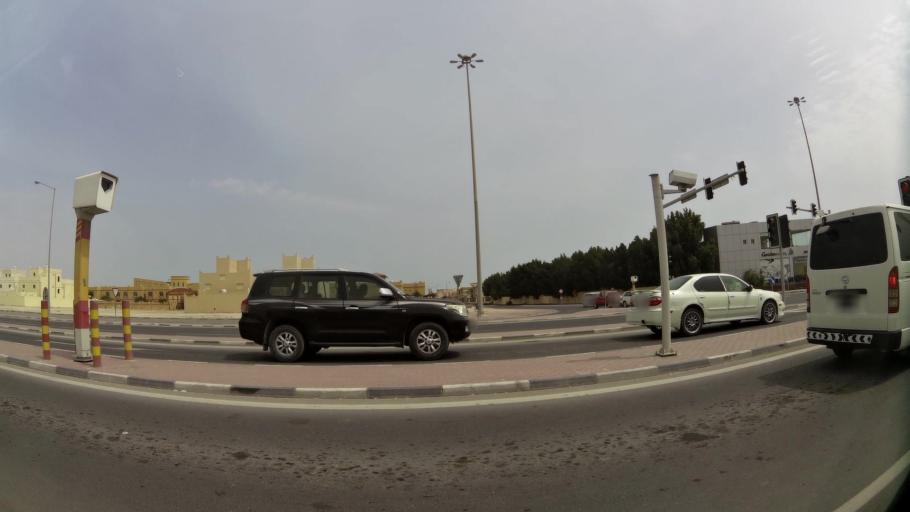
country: QA
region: Baladiyat ad Dawhah
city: Doha
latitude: 25.2385
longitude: 51.4978
